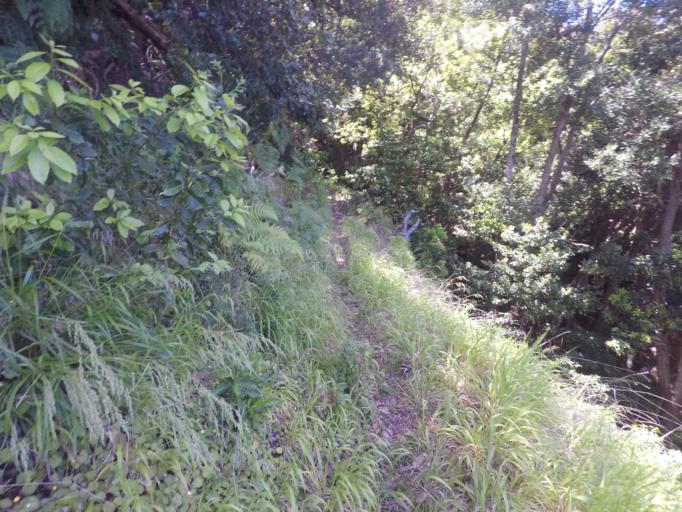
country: PT
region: Madeira
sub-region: Porto Moniz
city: Porto Moniz
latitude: 32.8322
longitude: -17.1373
